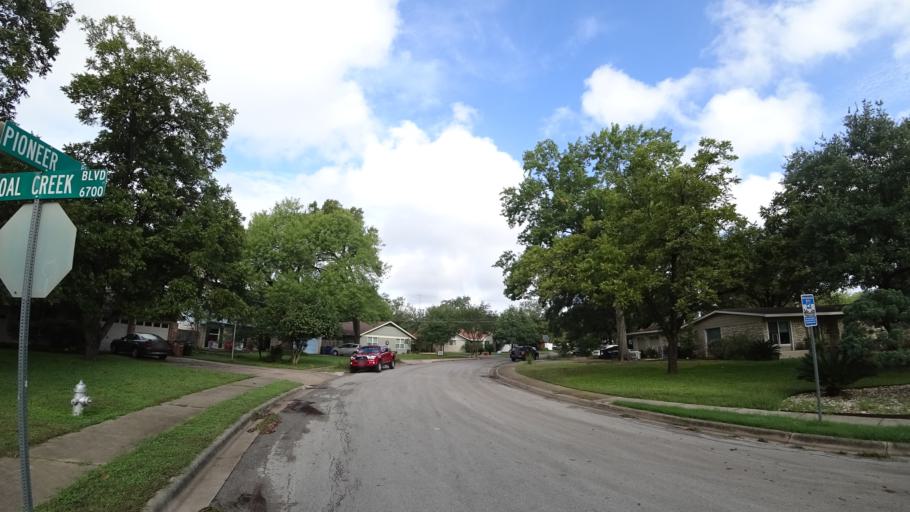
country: US
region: Texas
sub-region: Travis County
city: West Lake Hills
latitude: 30.3483
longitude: -97.7459
